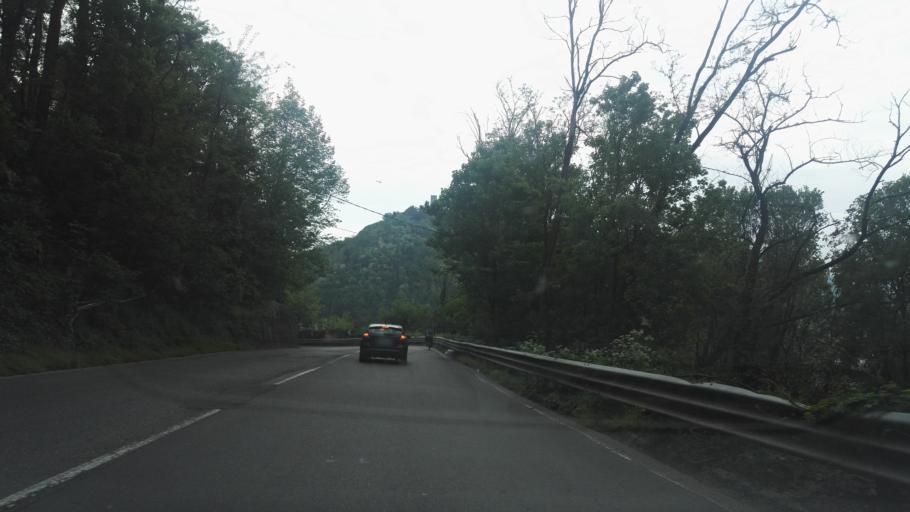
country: IT
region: Lombardy
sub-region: Provincia di Como
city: Lipomo
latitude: 45.7925
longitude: 9.0999
